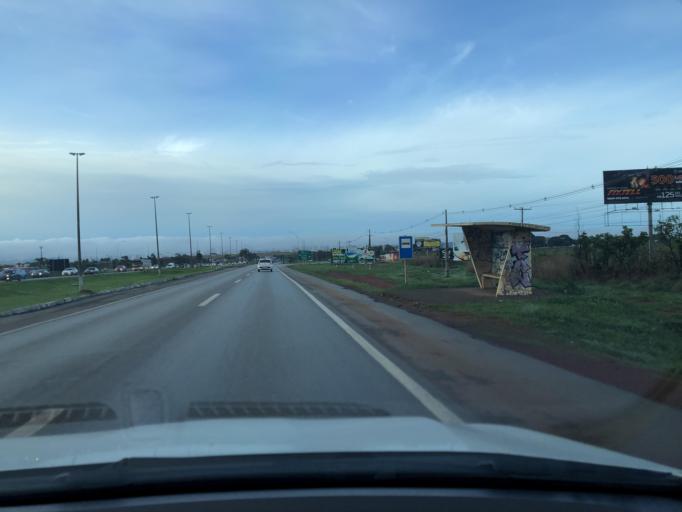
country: BR
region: Goias
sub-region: Luziania
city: Luziania
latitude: -16.0444
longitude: -47.9807
